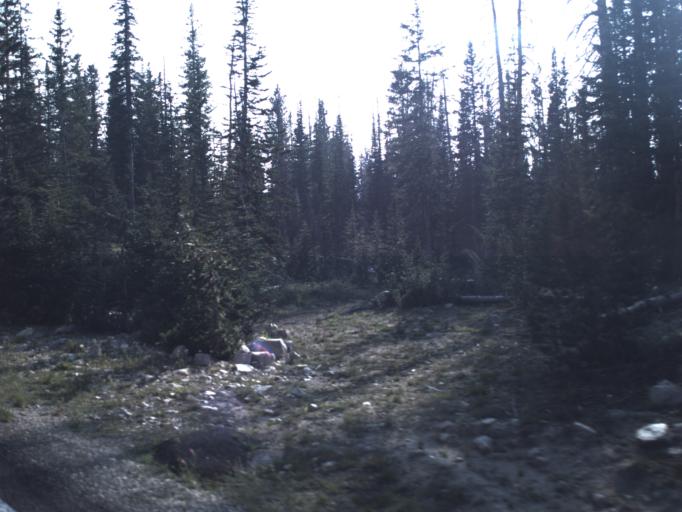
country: US
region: Utah
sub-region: Summit County
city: Kamas
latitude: 40.7247
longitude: -110.8648
